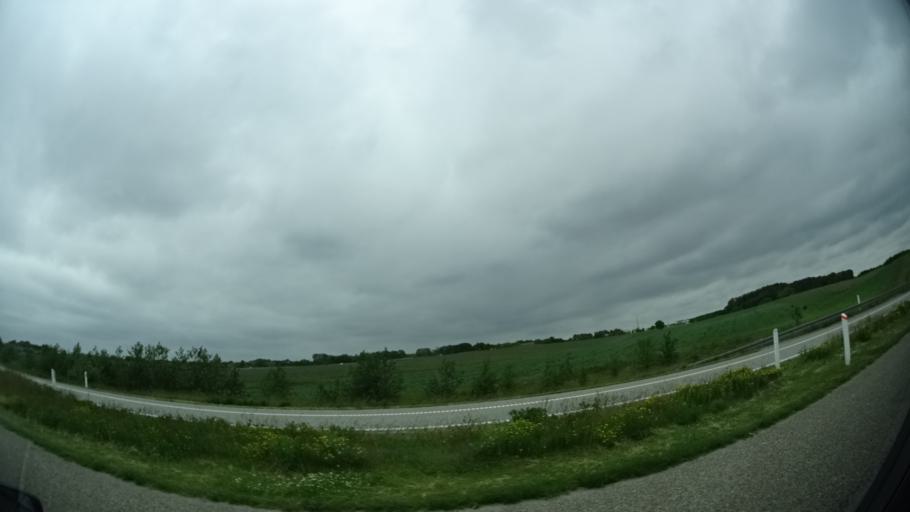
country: DK
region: Central Jutland
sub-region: Arhus Kommune
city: Hjortshoj
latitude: 56.2351
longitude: 10.2701
